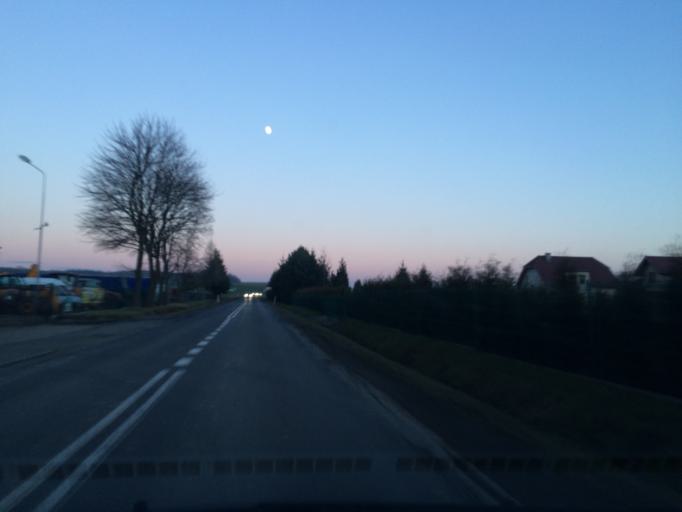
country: PL
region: Lower Silesian Voivodeship
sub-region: Powiat zlotoryjski
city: Zagrodno
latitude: 51.1208
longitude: 15.8236
